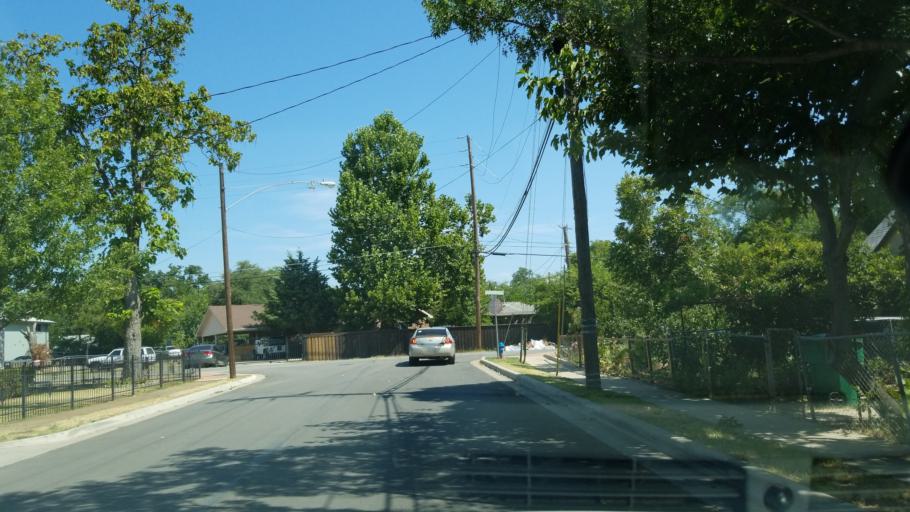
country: US
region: Texas
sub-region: Dallas County
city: Cockrell Hill
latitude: 32.7420
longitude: -96.8886
